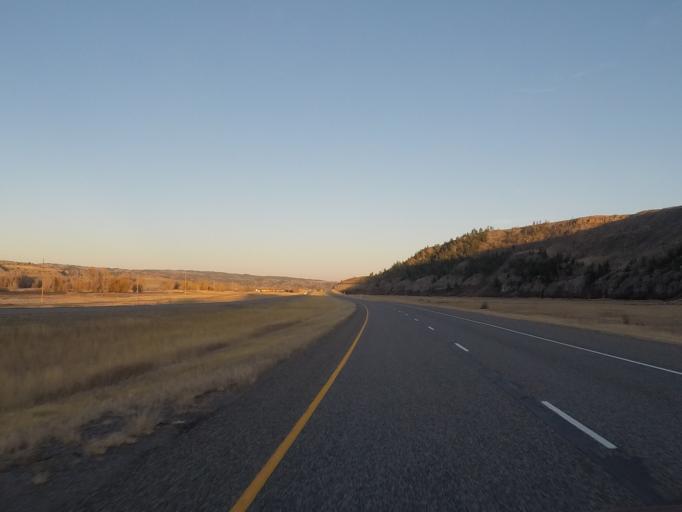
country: US
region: Montana
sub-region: Sweet Grass County
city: Big Timber
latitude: 45.7321
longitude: -109.7426
